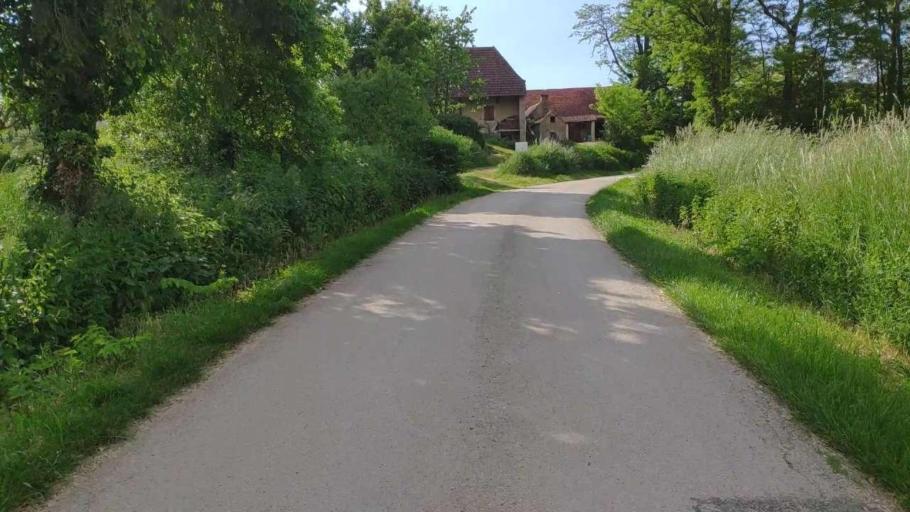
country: FR
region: Franche-Comte
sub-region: Departement du Jura
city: Bletterans
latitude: 46.8194
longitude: 5.3669
